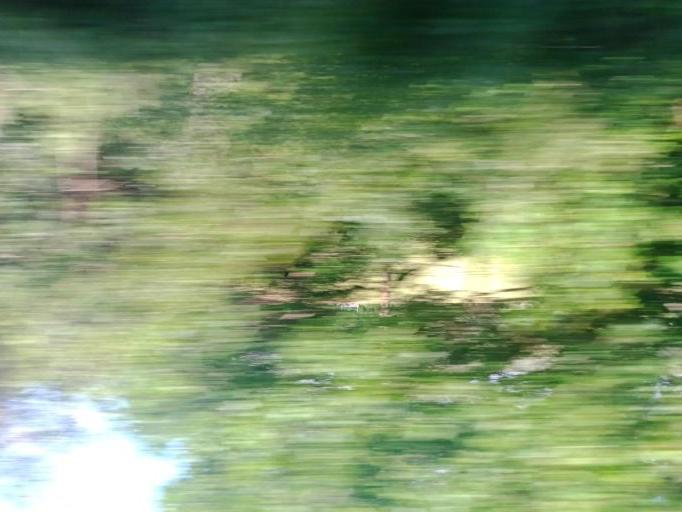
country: GB
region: Wales
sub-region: Gwynedd
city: Aber
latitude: 53.2309
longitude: -4.0463
